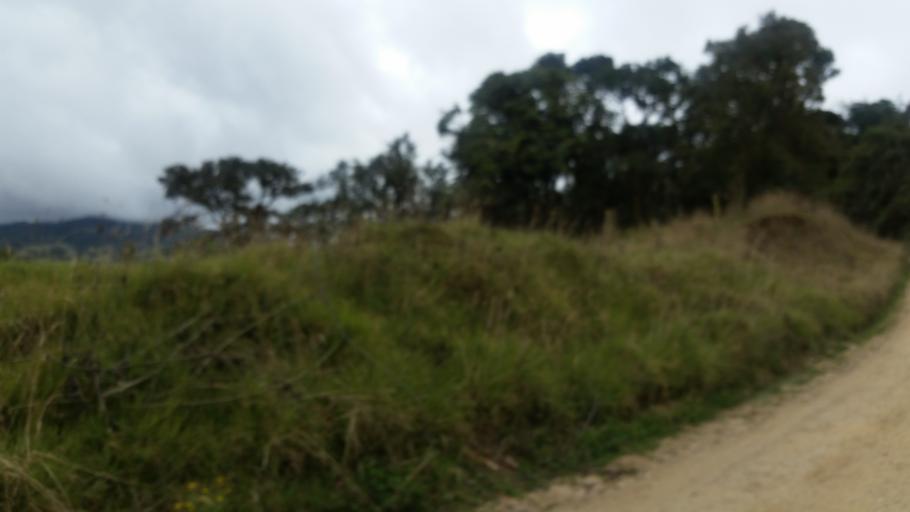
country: CO
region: Cundinamarca
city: La Calera
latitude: 4.7132
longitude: -73.9382
